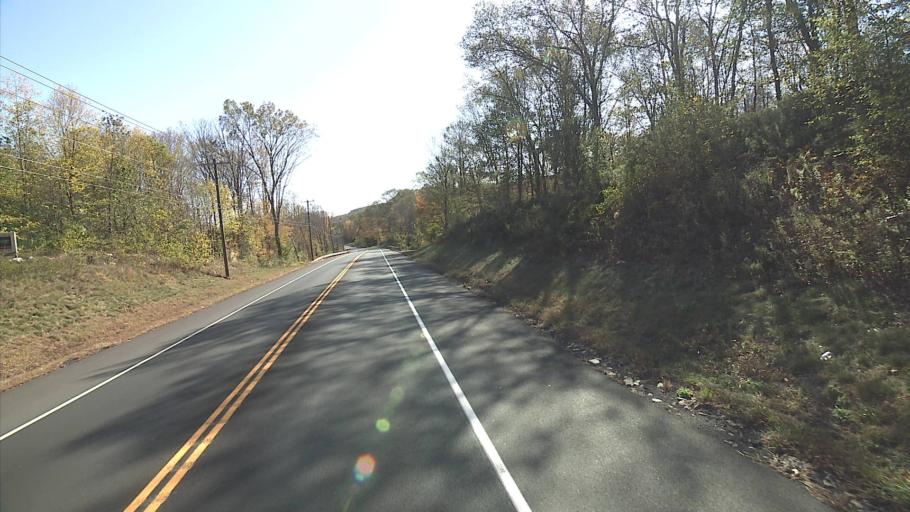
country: US
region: Connecticut
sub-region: Tolland County
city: Coventry Lake
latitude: 41.7300
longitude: -72.3254
